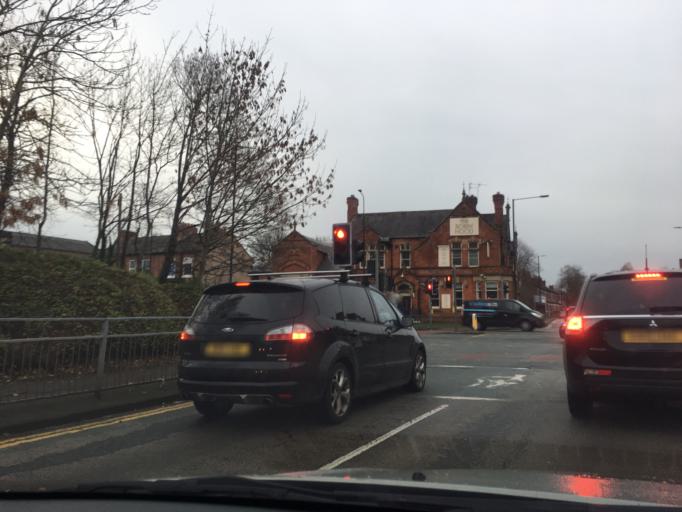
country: GB
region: England
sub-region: Trafford
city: Stretford
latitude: 53.4457
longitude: -2.3134
